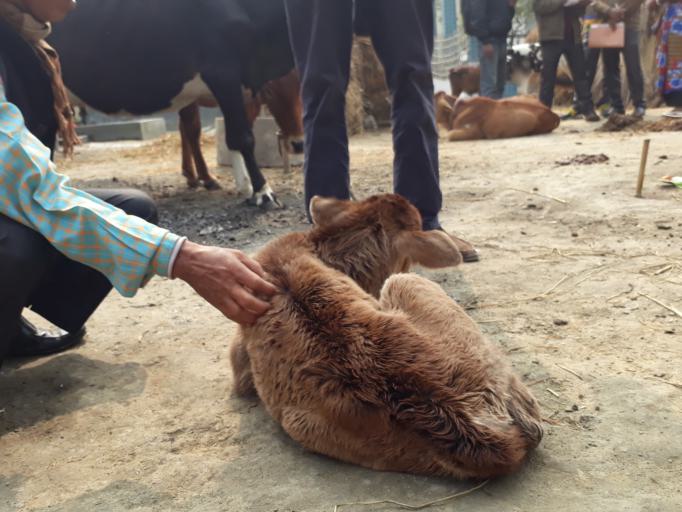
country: BD
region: Khulna
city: Kesabpur
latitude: 22.7904
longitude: 89.2741
